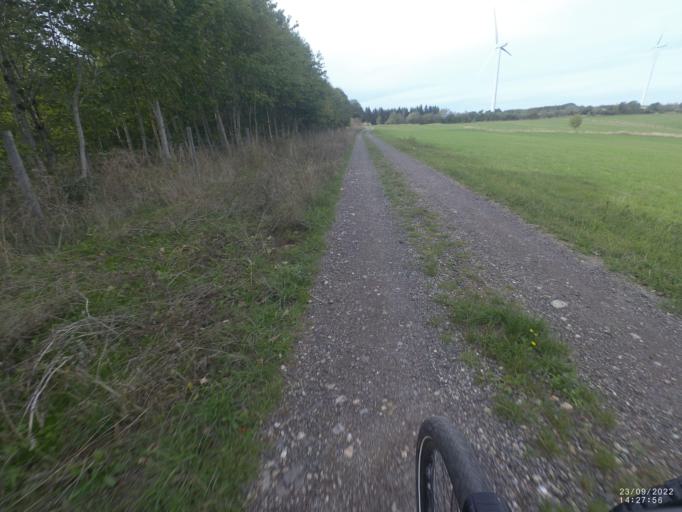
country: DE
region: Rheinland-Pfalz
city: Hinterweiler
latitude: 50.2339
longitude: 6.7704
